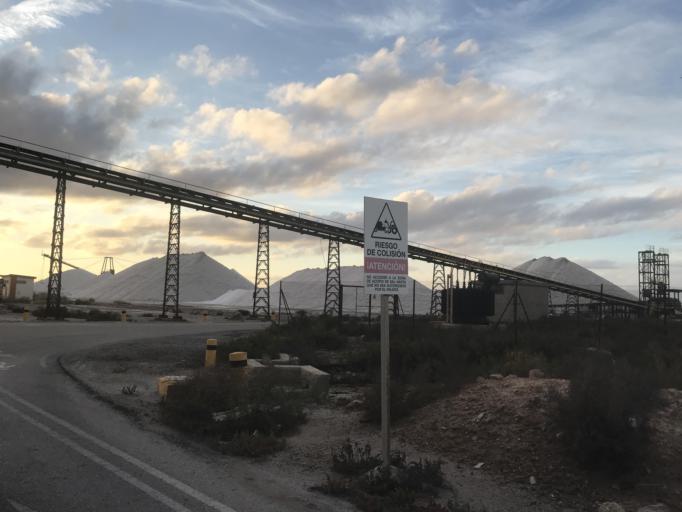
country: ES
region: Valencia
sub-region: Provincia de Alicante
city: Torrevieja
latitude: 37.9791
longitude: -0.6987
